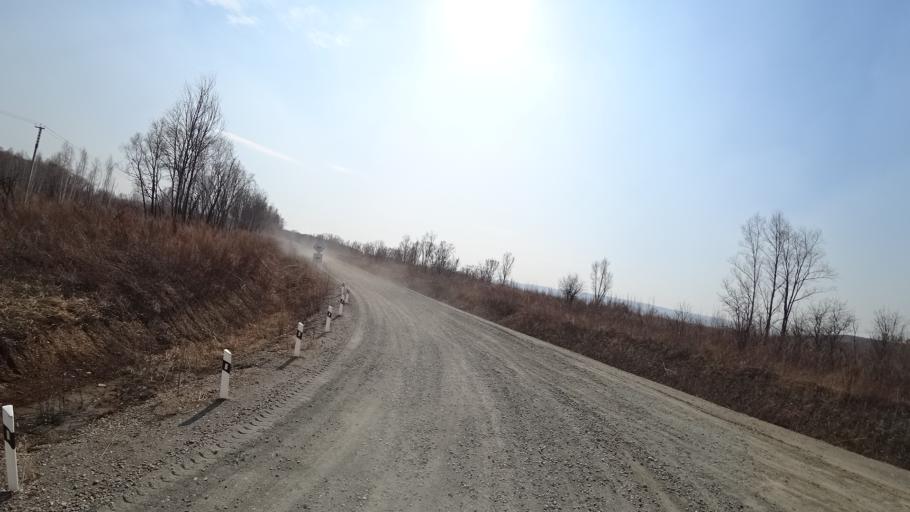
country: RU
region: Amur
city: Novobureyskiy
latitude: 49.8278
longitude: 129.9889
